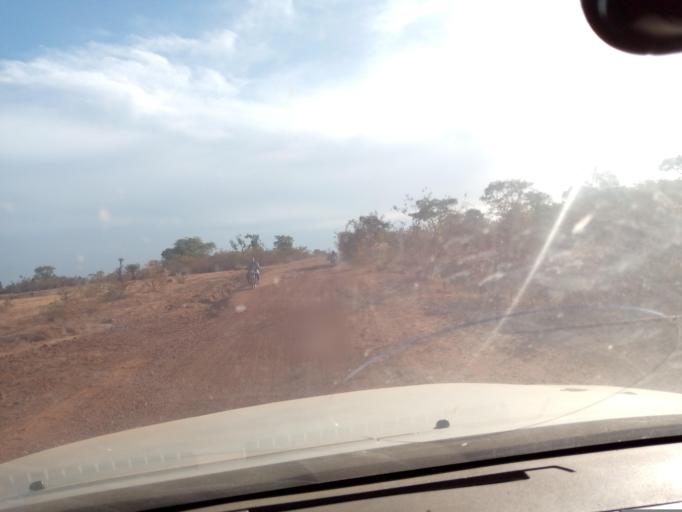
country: ML
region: Sikasso
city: Sikasso
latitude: 11.4116
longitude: -5.5700
